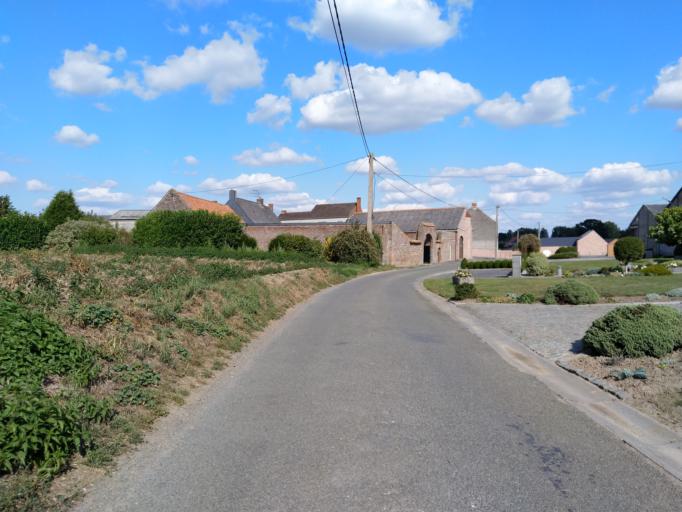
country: BE
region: Wallonia
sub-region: Province du Hainaut
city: Lens
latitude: 50.5245
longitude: 3.8434
